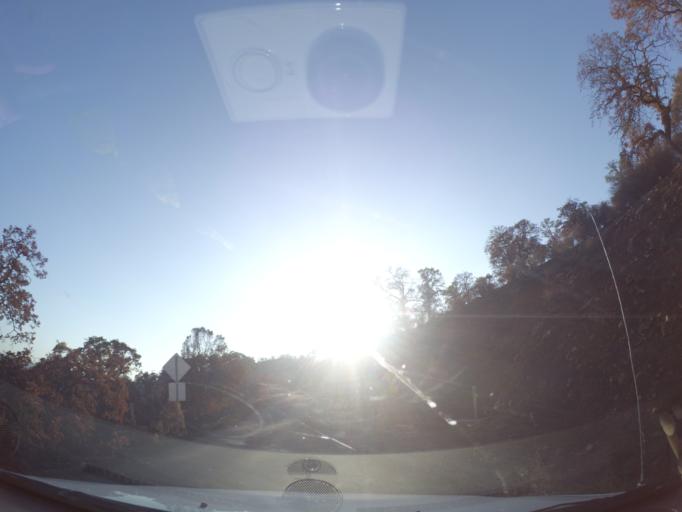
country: US
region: California
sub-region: Mariposa County
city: Mariposa
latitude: 37.5065
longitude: -120.1002
